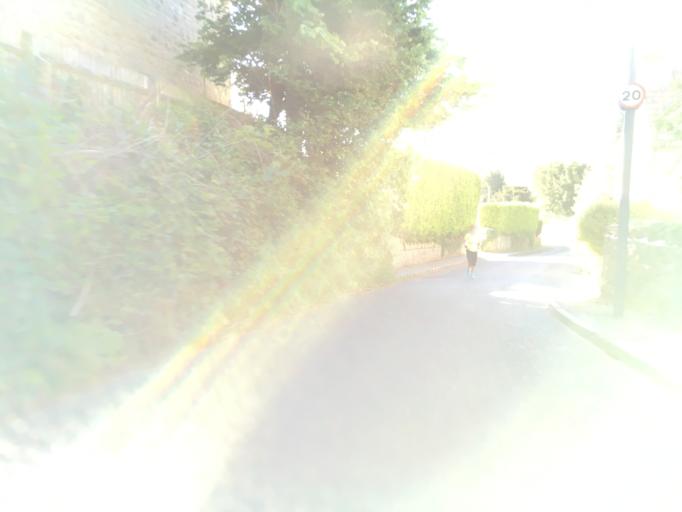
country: GB
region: England
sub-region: North Somerset
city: Clevedon
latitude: 51.4560
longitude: -2.8307
